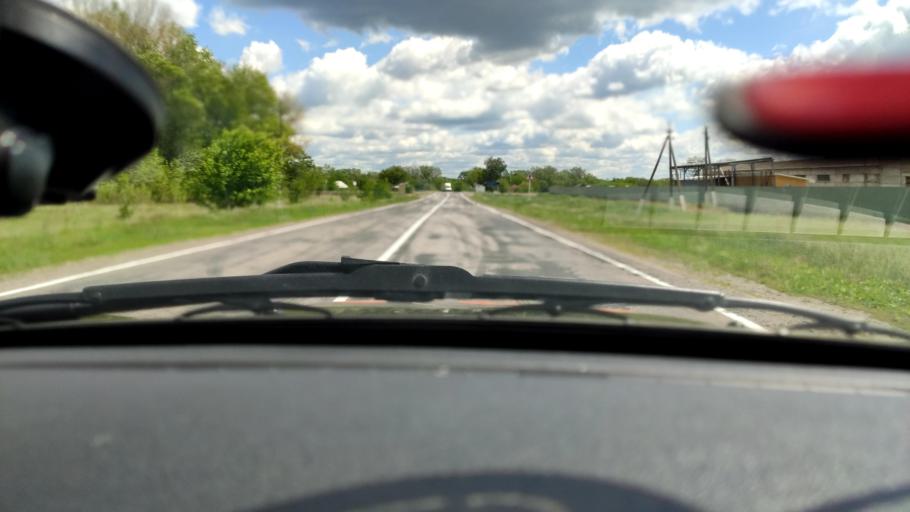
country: RU
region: Voronezj
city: Ostrogozhsk
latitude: 51.0556
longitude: 38.9072
